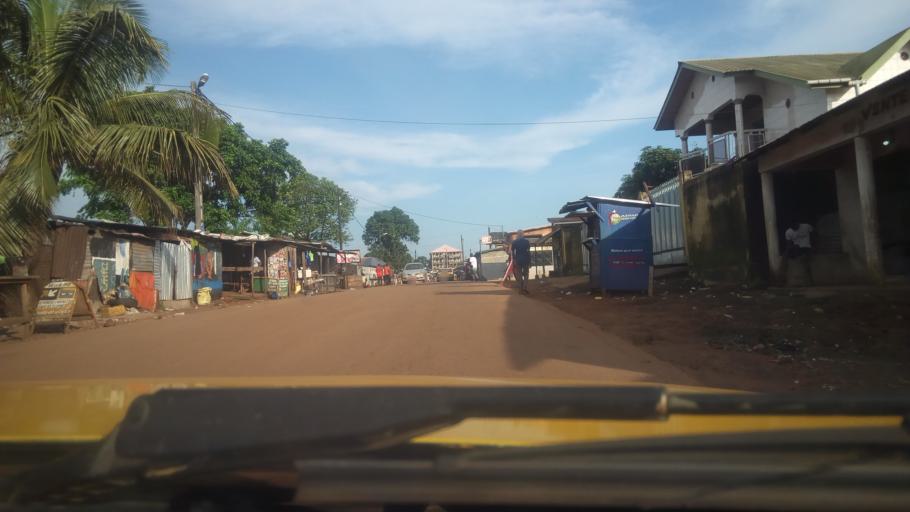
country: GN
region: Conakry
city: Conakry
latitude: 9.6210
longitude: -13.6090
